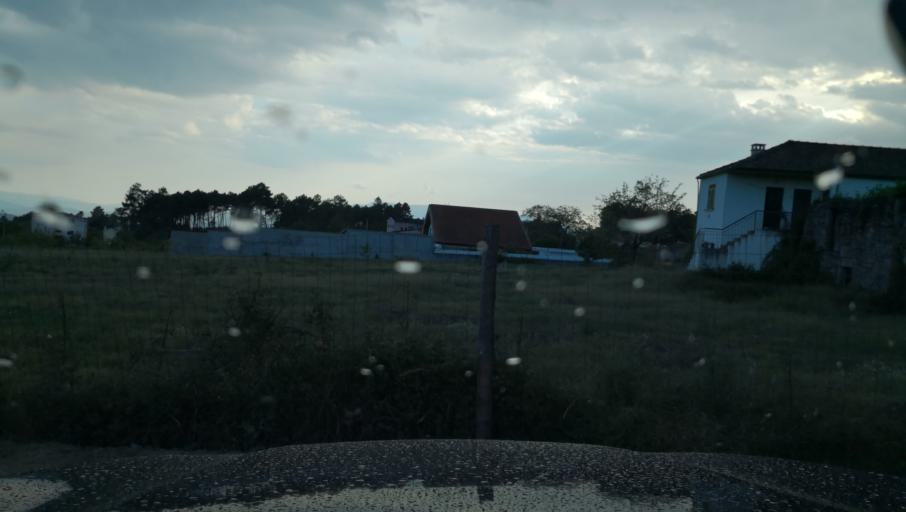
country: PT
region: Vila Real
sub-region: Vila Real
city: Vila Real
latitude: 41.3193
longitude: -7.6816
